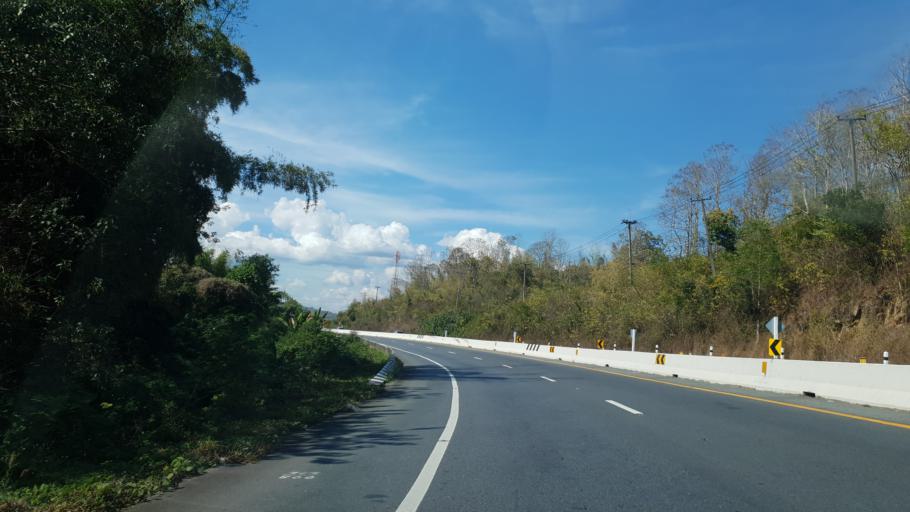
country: TH
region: Phrae
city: Den Chai
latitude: 17.9181
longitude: 100.0689
